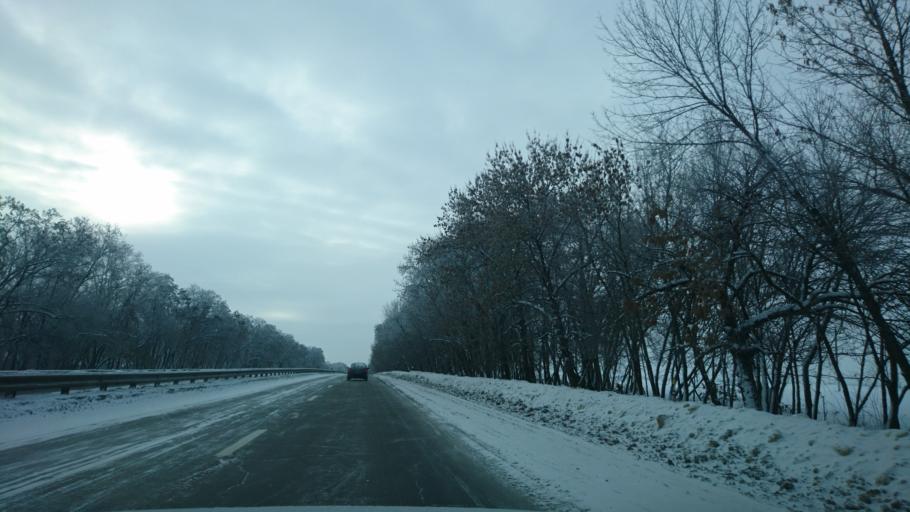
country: RU
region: Belgorod
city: Mayskiy
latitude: 50.4784
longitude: 36.4058
